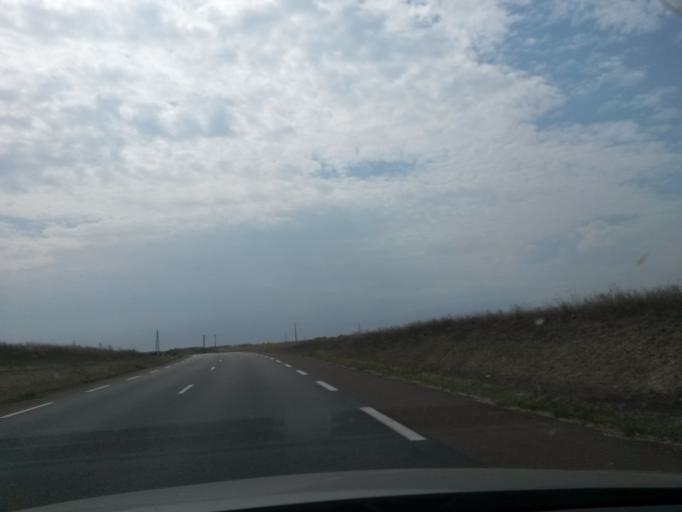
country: FR
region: Poitou-Charentes
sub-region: Departement de la Charente-Maritime
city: Saint-Xandre
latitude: 46.2134
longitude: -1.0910
